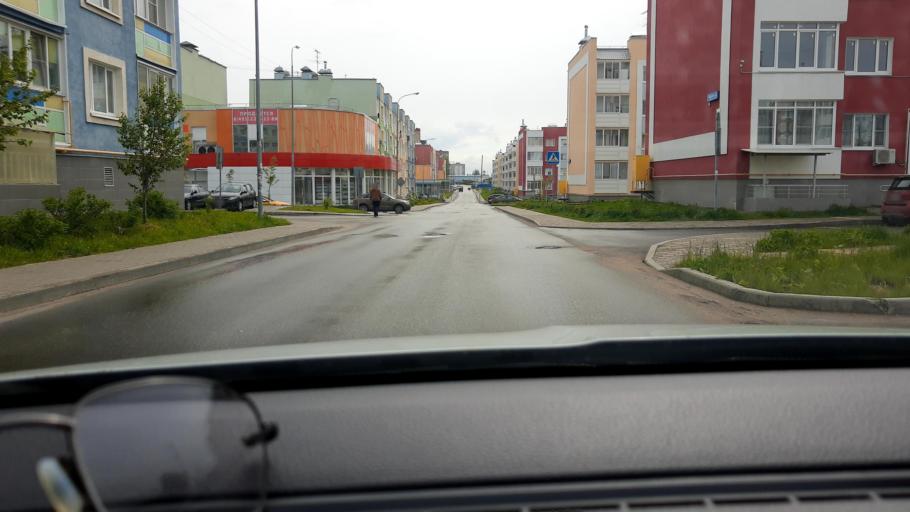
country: RU
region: Moskovskaya
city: Dedovsk
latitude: 55.8411
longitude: 37.1271
